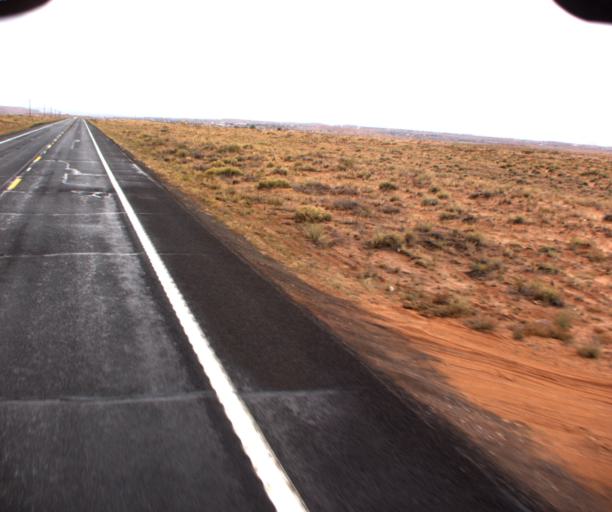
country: US
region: Arizona
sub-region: Coconino County
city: Tuba City
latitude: 36.1348
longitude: -111.1774
